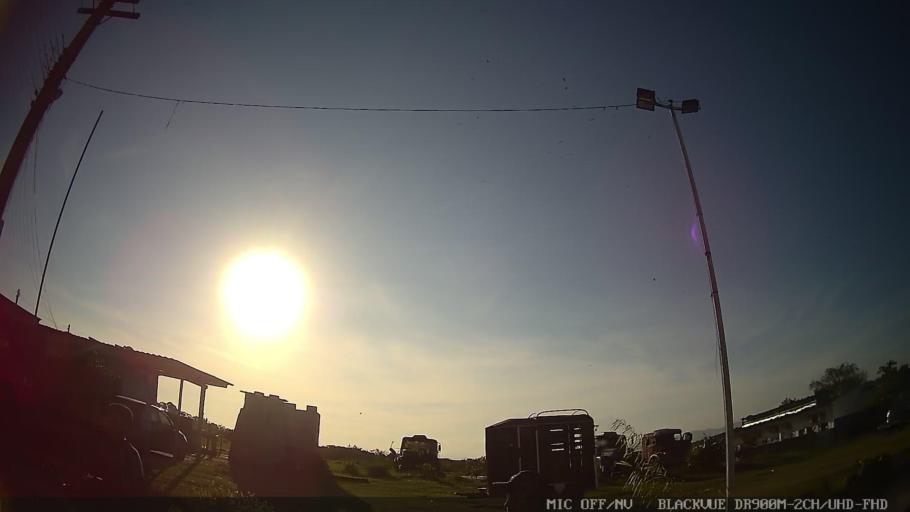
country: BR
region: Sao Paulo
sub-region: Guaruja
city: Guaruja
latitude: -23.9733
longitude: -46.2516
